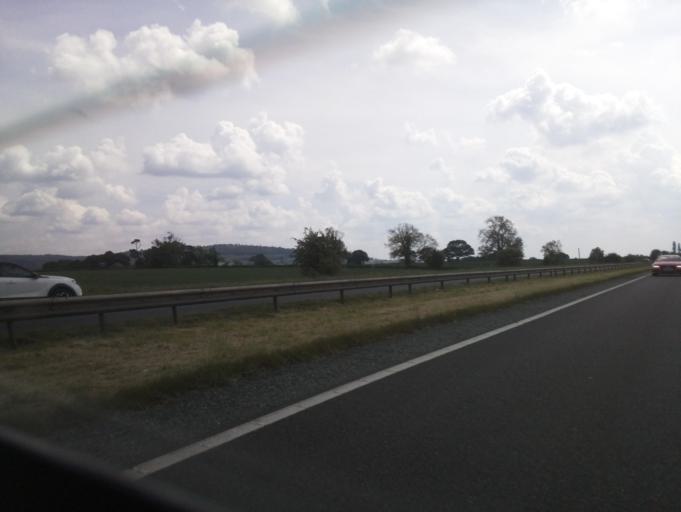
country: GB
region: England
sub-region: North Yorkshire
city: Thirsk
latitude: 54.3056
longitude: -1.3372
